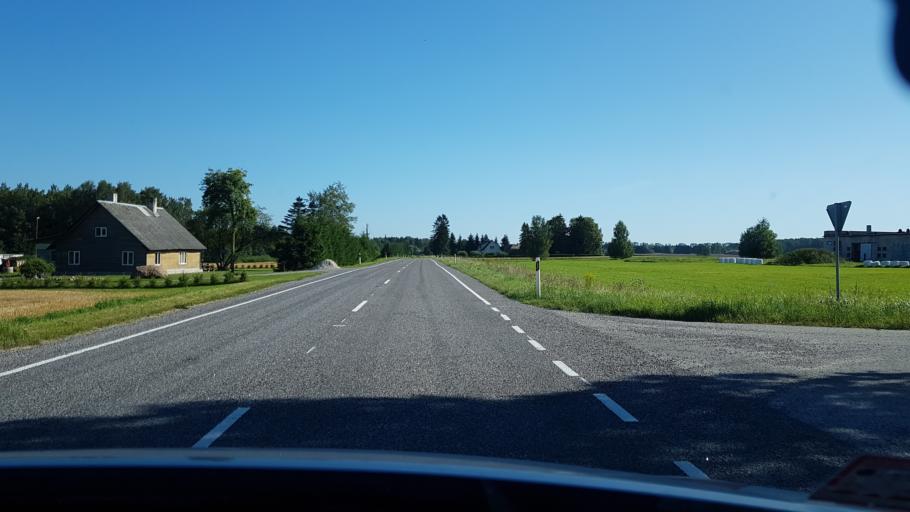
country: EE
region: Tartu
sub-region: Tartu linn
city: Tartu
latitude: 58.4584
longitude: 26.6829
